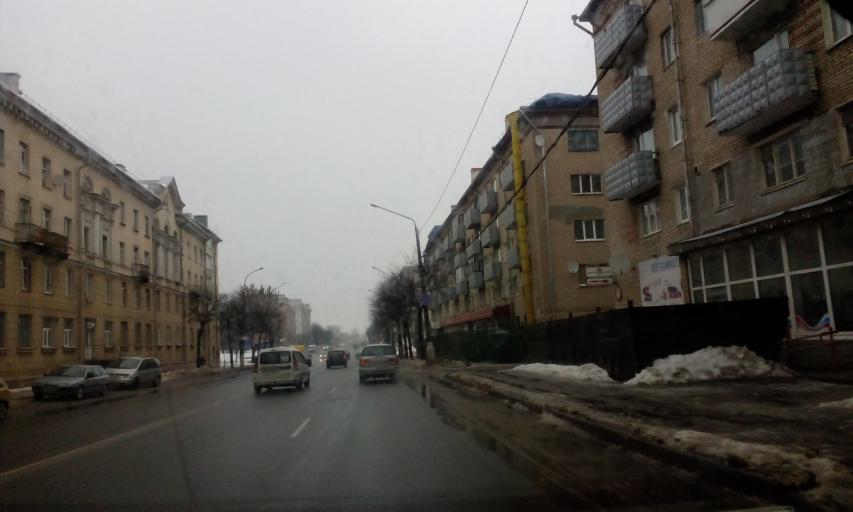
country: BY
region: Mogilev
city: Mahilyow
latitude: 53.9038
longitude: 30.3445
